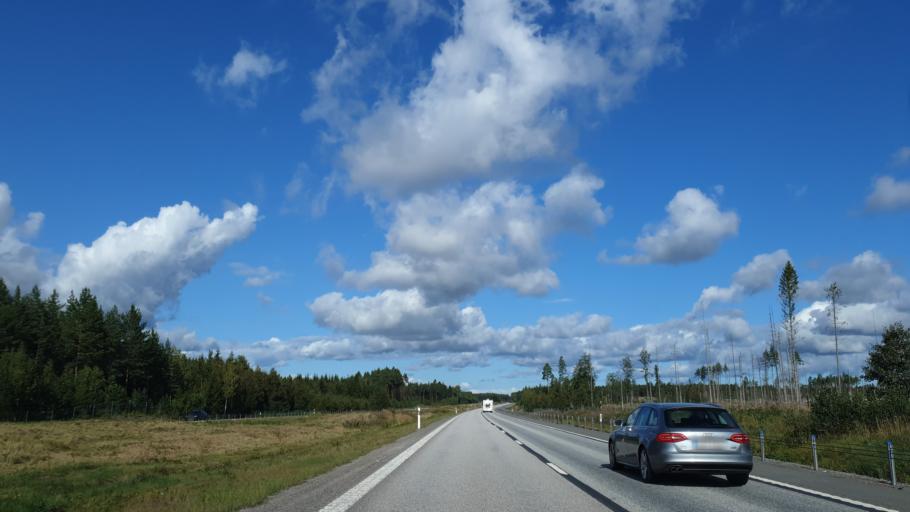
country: SE
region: Uppsala
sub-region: Tierps Kommun
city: Tierp
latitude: 60.2597
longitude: 17.5005
